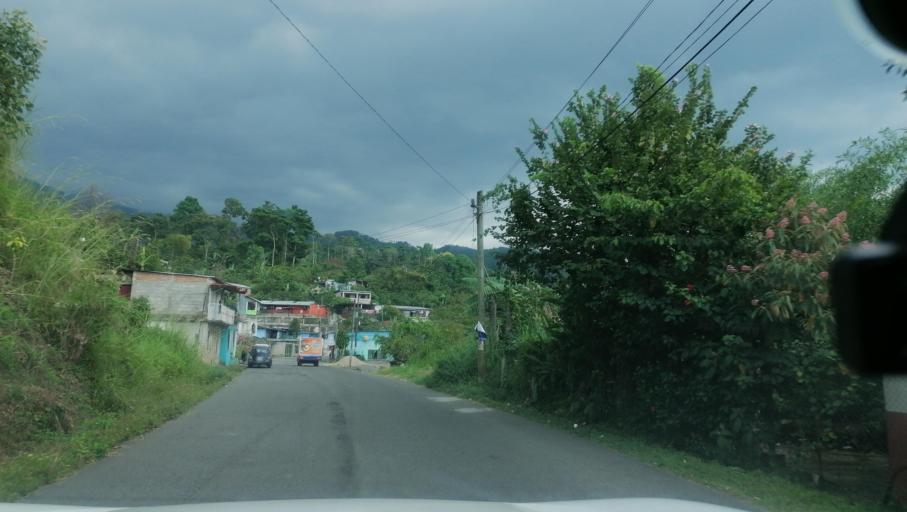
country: MX
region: Chiapas
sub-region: Cacahoatan
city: Benito Juarez
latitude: 15.0744
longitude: -92.1972
